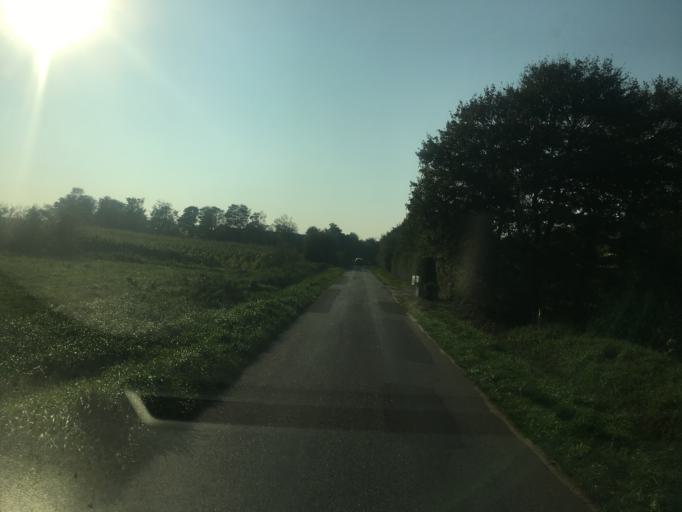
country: DE
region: Schleswig-Holstein
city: Ladelund
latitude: 54.9238
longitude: 9.0292
